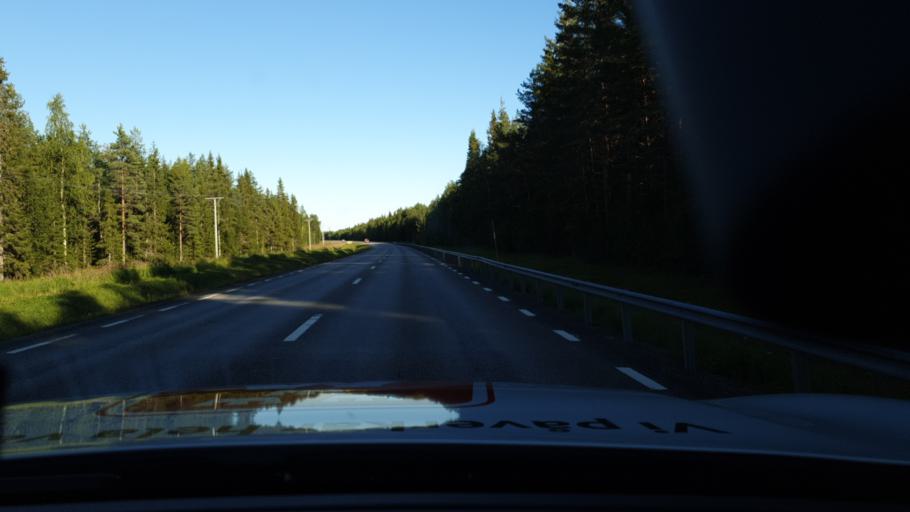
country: SE
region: Norrbotten
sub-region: Pitea Kommun
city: Rosvik
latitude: 65.5866
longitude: 21.6688
